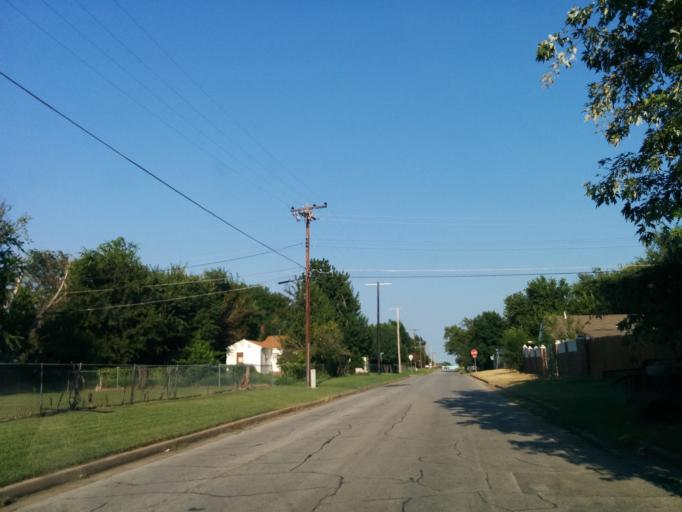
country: US
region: Oklahoma
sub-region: Tulsa County
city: Tulsa
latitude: 36.1662
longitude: -95.9095
